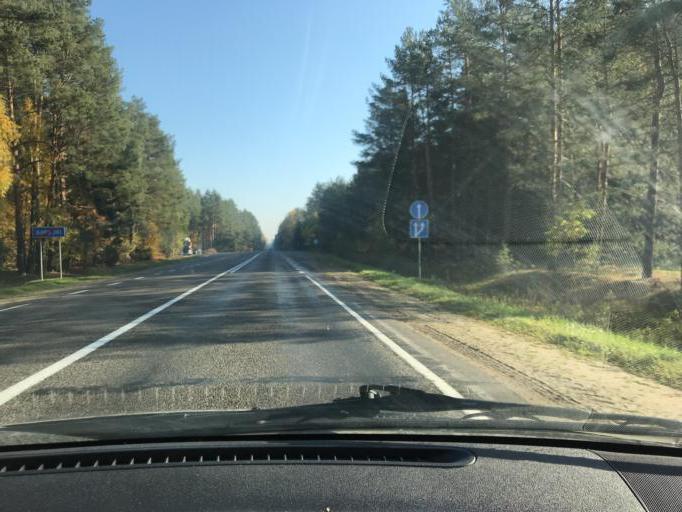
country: BY
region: Brest
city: Baranovichi
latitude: 52.9223
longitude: 25.9885
